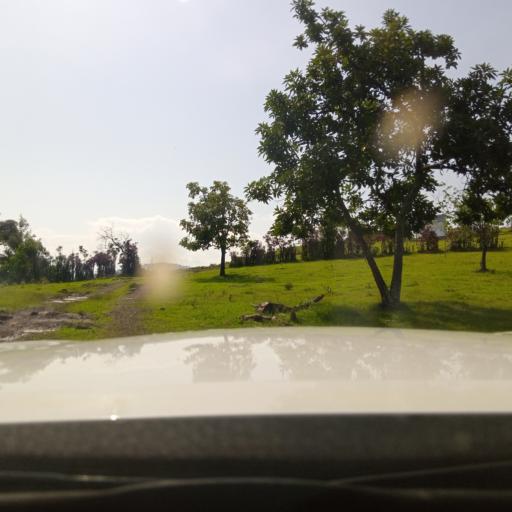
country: ET
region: Oromiya
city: Agaro
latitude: 7.9203
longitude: 36.7990
